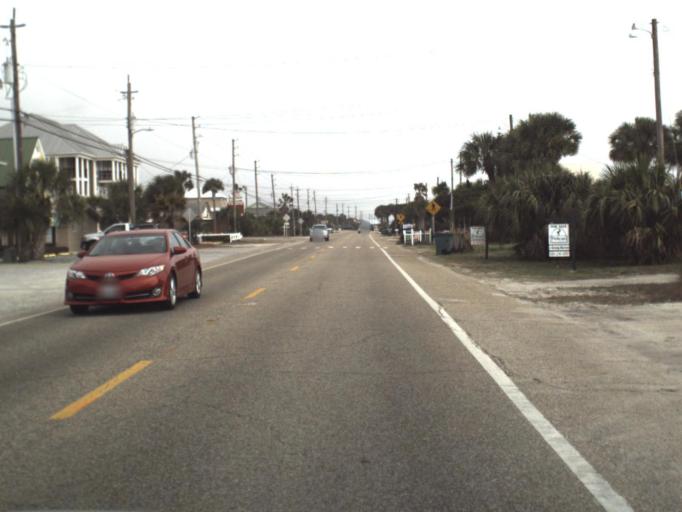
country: US
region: Florida
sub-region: Bay County
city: Laguna Beach
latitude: 30.2561
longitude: -85.9615
